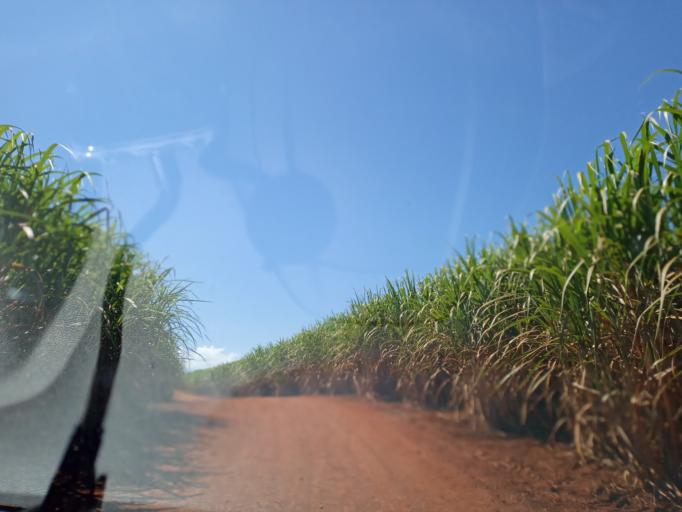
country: BR
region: Goias
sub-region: Itumbiara
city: Itumbiara
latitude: -18.4409
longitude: -49.1412
